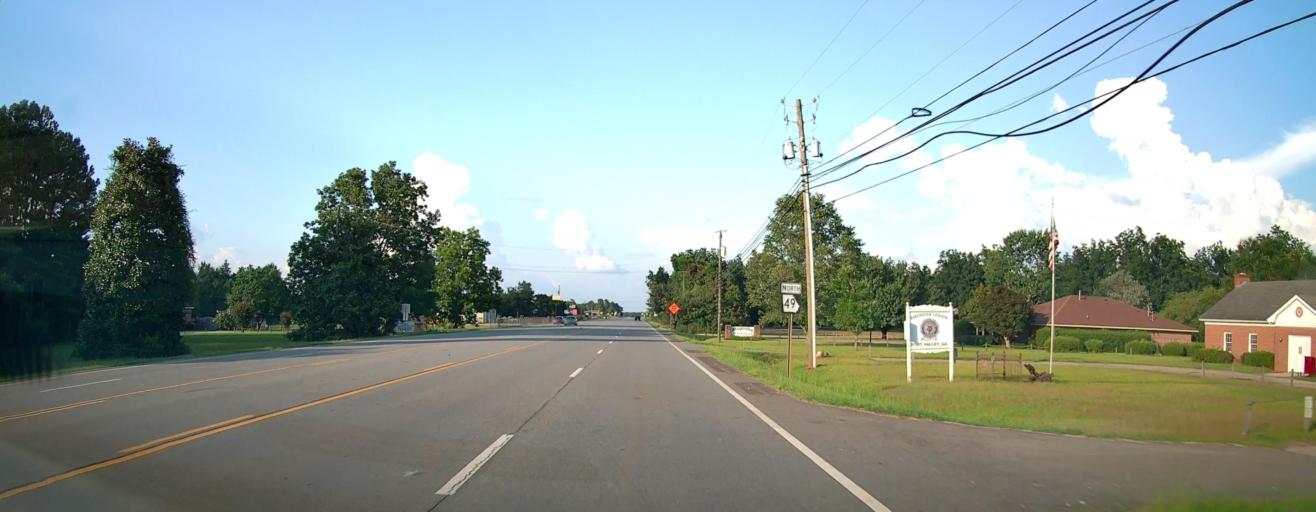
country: US
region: Georgia
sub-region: Peach County
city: Fort Valley
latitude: 32.5723
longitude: -83.8710
